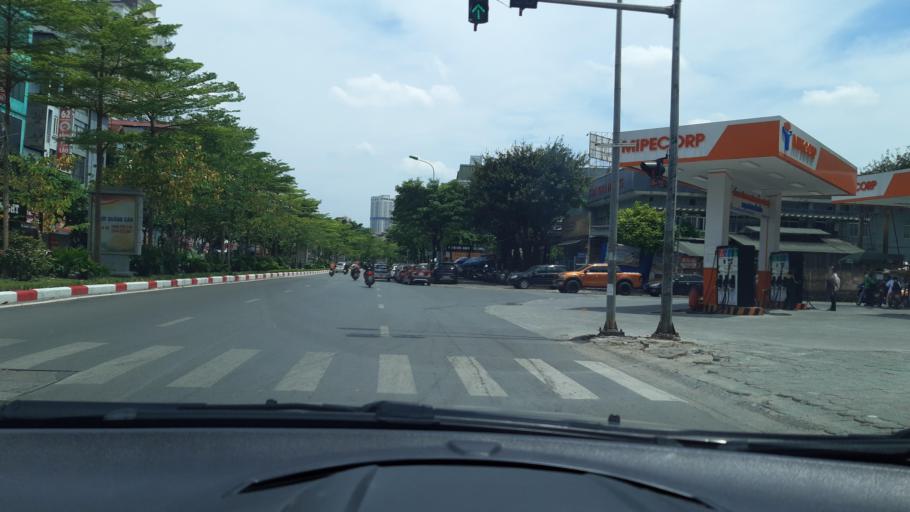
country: VN
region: Ha Noi
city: Cau Giay
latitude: 21.0402
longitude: 105.7903
